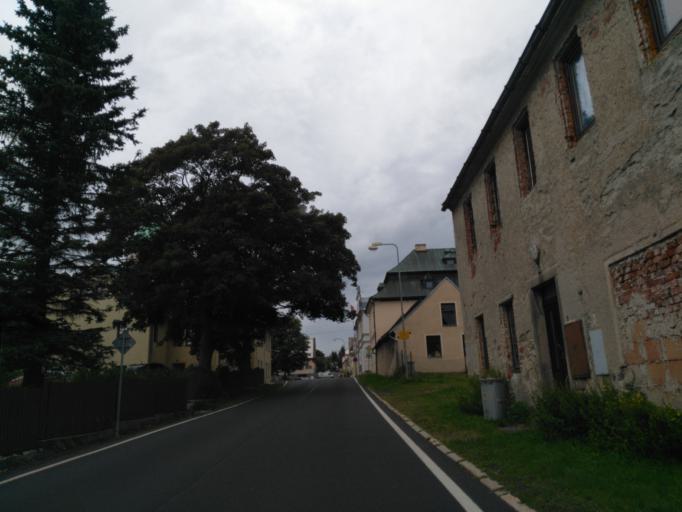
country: CZ
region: Karlovarsky
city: Abertamy
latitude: 50.3895
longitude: 12.7714
